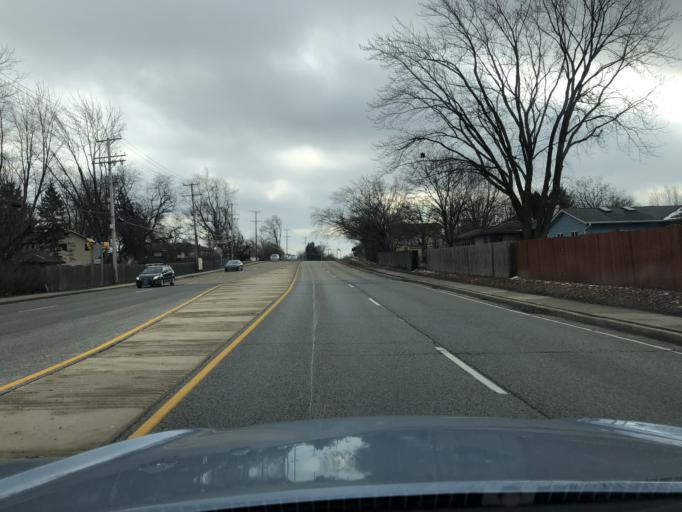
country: US
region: Illinois
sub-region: Cook County
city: Elk Grove Village
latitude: 42.0103
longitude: -88.0035
